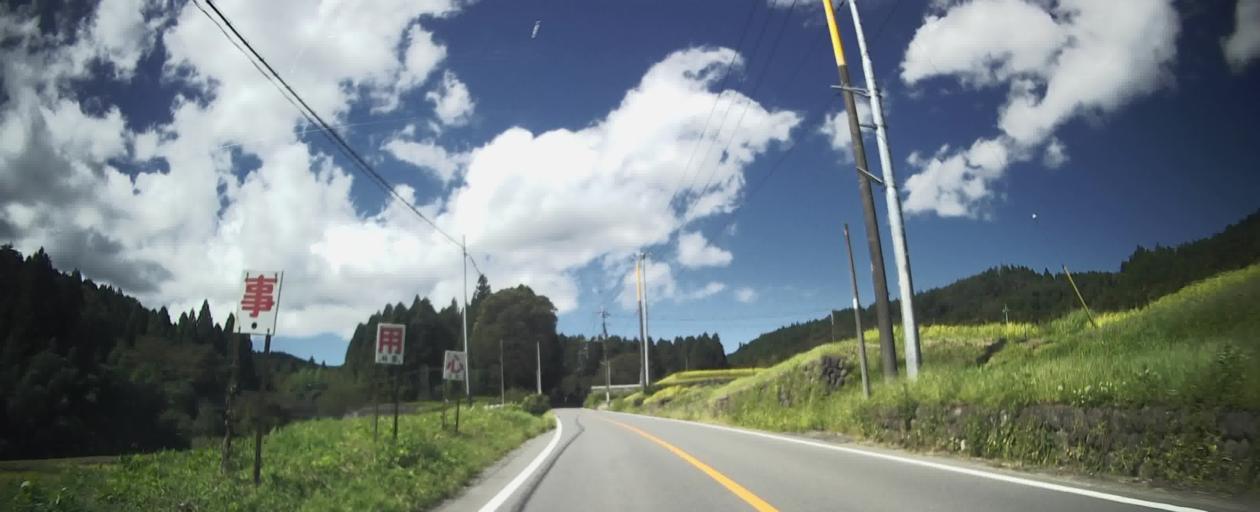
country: JP
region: Gunma
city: Kanekomachi
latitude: 36.4287
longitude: 138.9278
